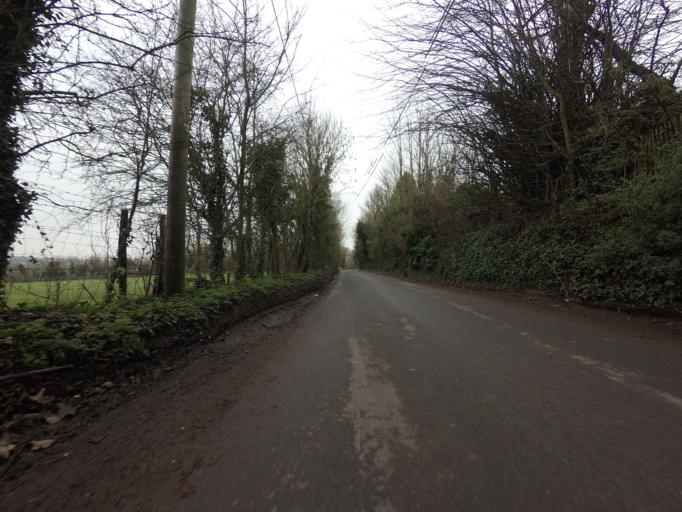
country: GB
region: England
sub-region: Kent
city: Eynsford
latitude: 51.3868
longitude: 0.2419
